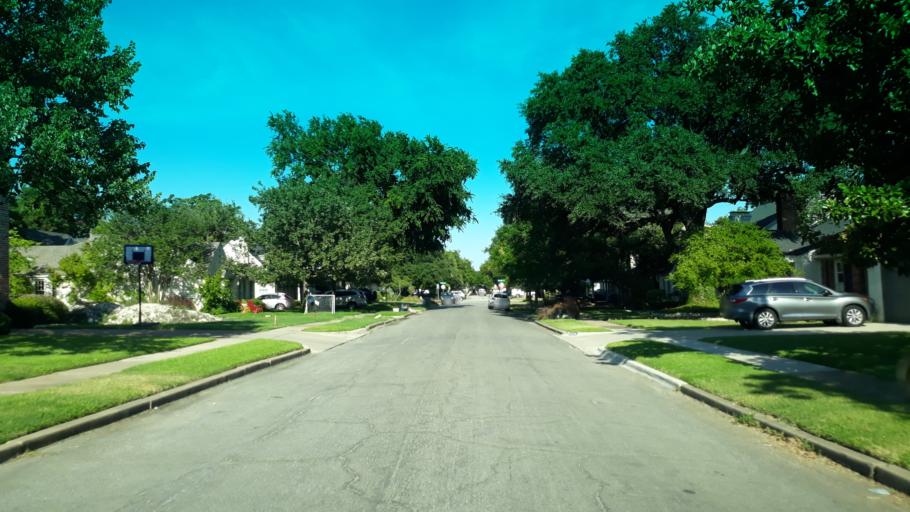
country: US
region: Texas
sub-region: Dallas County
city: Highland Park
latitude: 32.8308
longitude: -96.7629
